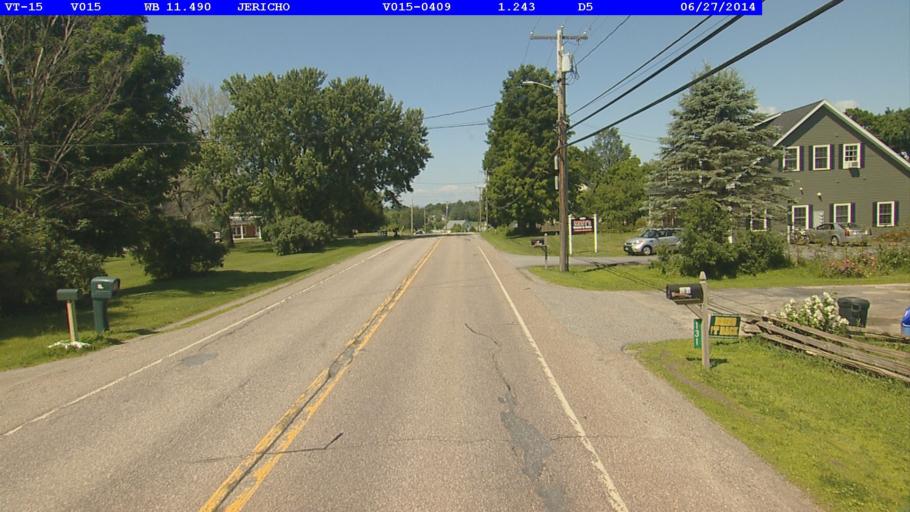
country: US
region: Vermont
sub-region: Chittenden County
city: Jericho
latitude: 44.5089
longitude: -72.9839
